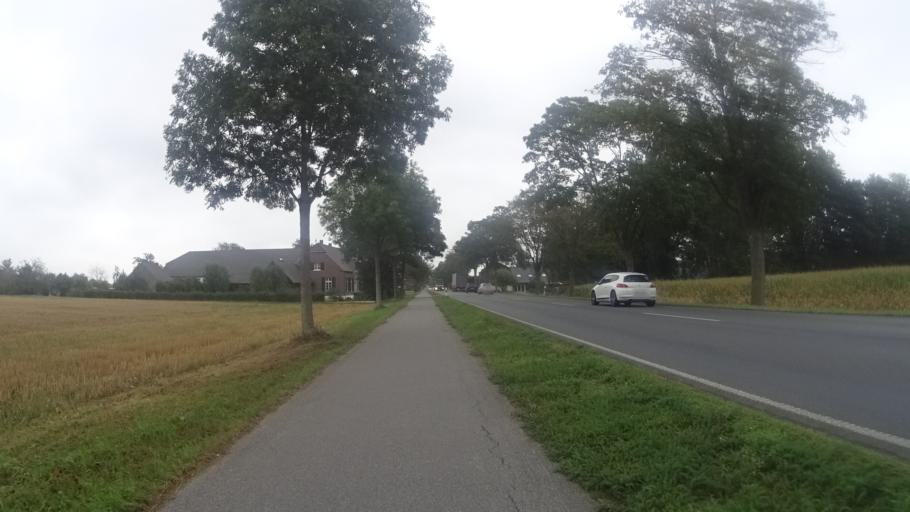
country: DE
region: North Rhine-Westphalia
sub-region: Regierungsbezirk Dusseldorf
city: Issum
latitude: 51.5251
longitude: 6.3846
